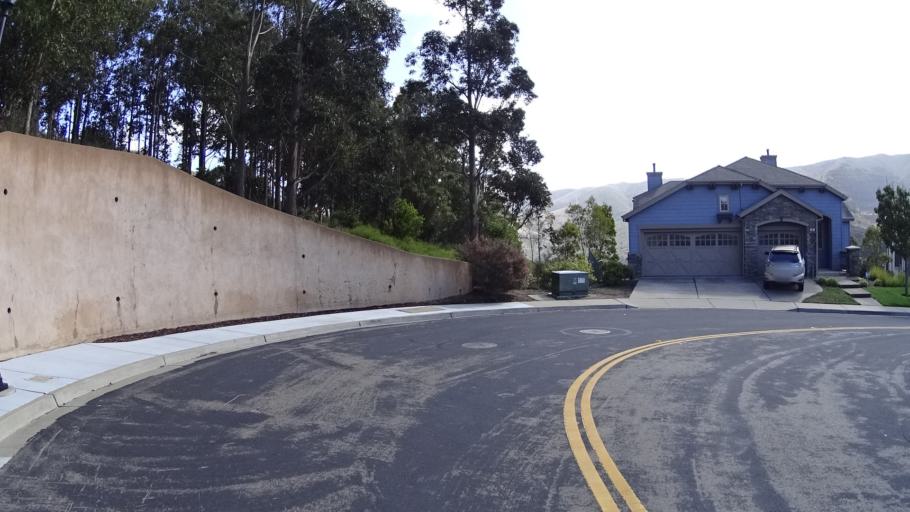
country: US
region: California
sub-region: San Mateo County
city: Brisbane
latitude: 37.6949
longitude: -122.4181
